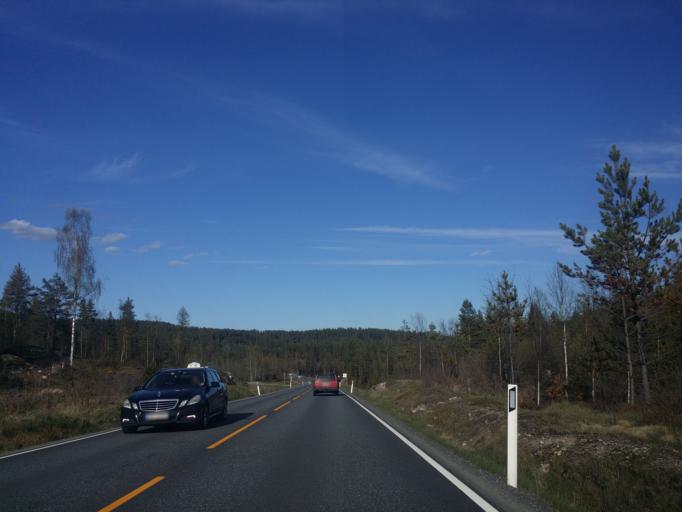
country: NO
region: Buskerud
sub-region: Kongsberg
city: Kongsberg
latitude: 59.6306
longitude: 9.5093
